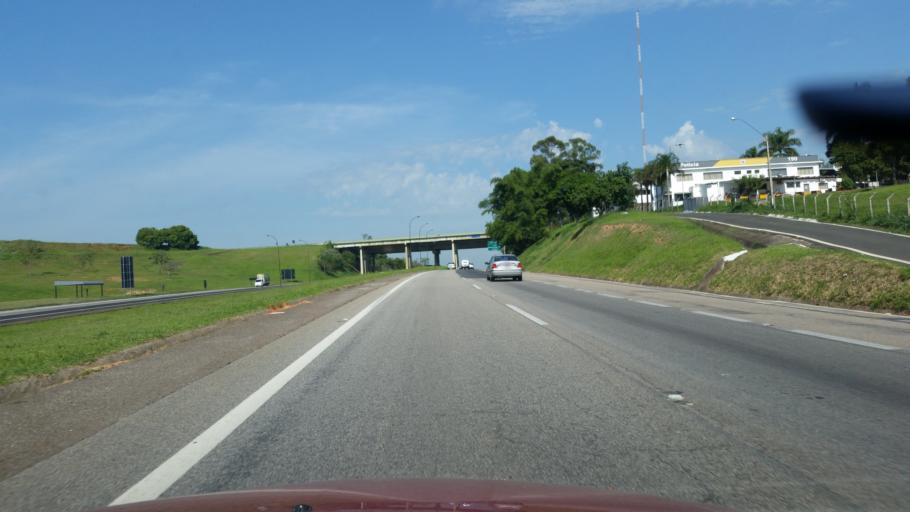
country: BR
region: Sao Paulo
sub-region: Tatui
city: Tatui
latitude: -23.2830
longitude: -47.8034
